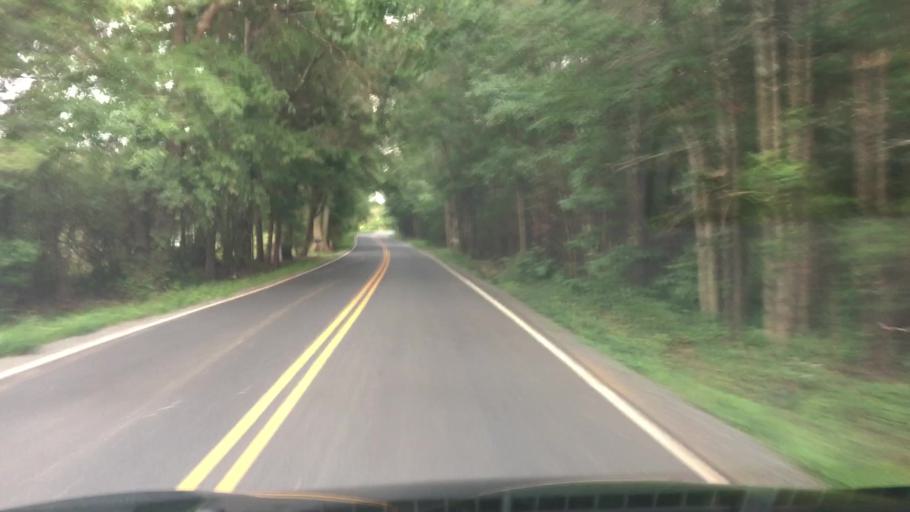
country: US
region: Virginia
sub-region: Fauquier County
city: Bealeton
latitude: 38.5877
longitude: -77.7034
